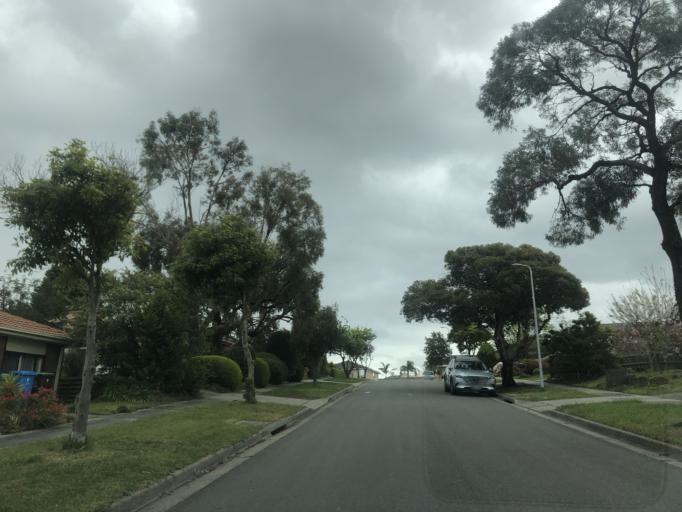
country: AU
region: Victoria
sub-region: Casey
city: Endeavour Hills
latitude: -37.9803
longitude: 145.2554
